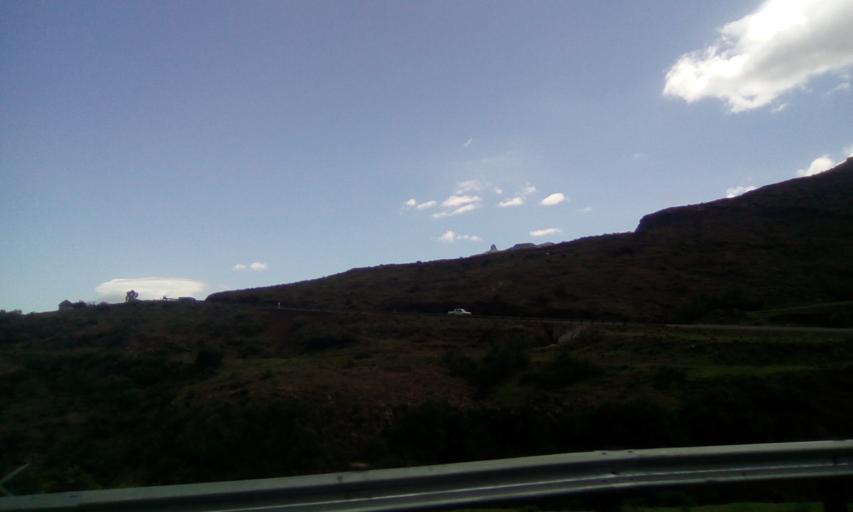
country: LS
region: Maseru
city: Nako
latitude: -29.6404
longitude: 27.7642
